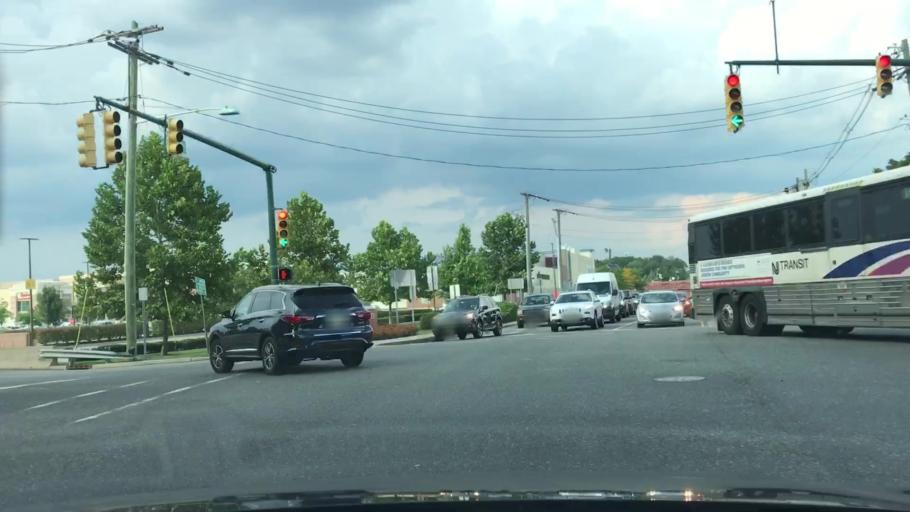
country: US
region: New Jersey
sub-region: Bergen County
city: Maywood
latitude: 40.9122
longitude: -74.0577
